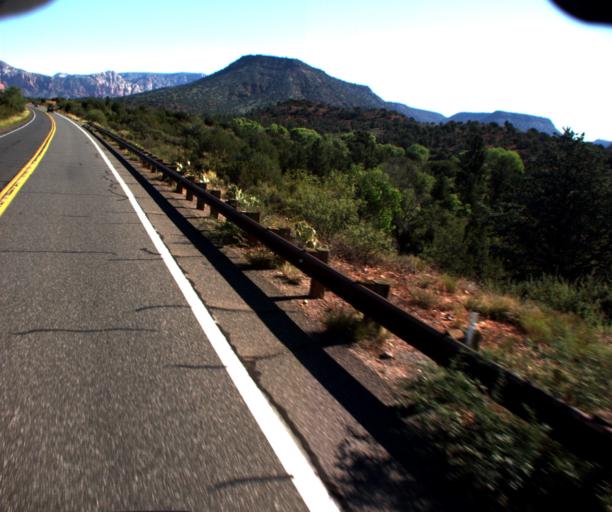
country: US
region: Arizona
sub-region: Yavapai County
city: Big Park
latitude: 34.7471
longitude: -111.7669
